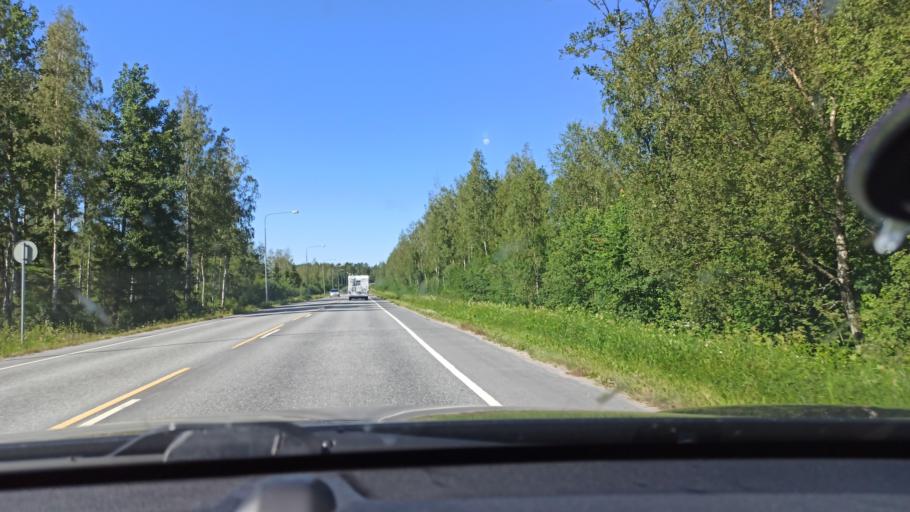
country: FI
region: Ostrobothnia
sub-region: Jakobstadsregionen
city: Jakobstad
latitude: 63.6609
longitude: 22.7096
